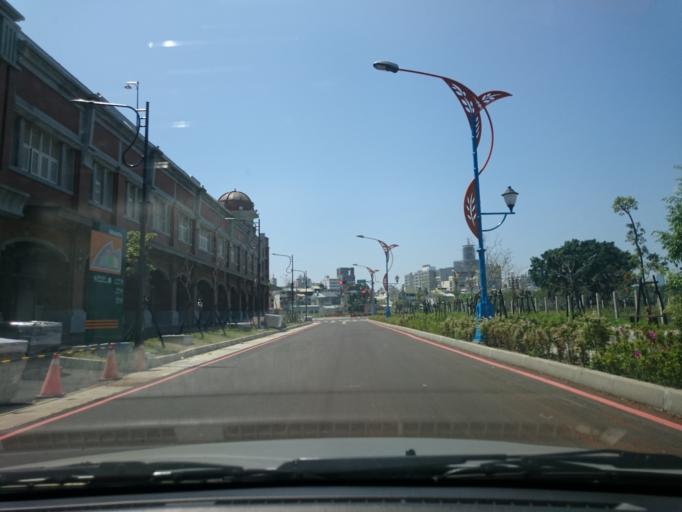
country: TW
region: Taiwan
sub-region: Taichung City
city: Taichung
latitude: 24.1349
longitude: 120.6940
